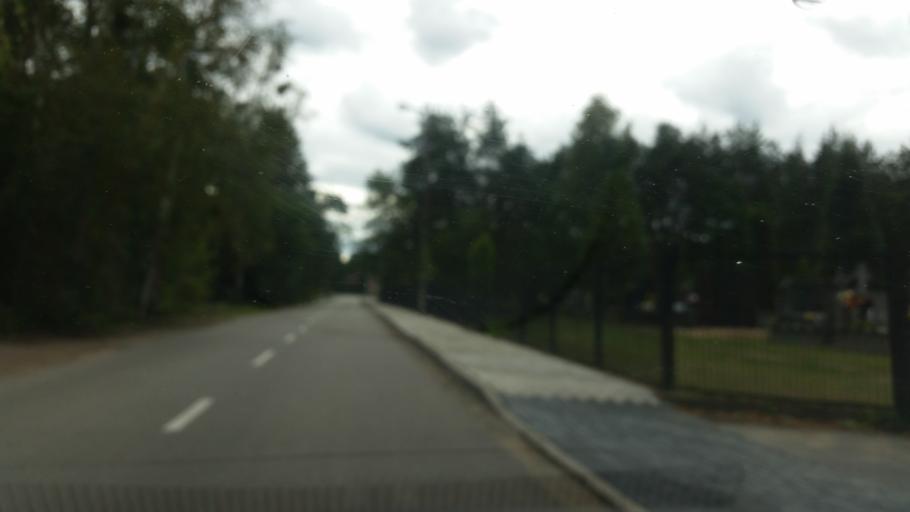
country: PL
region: Masovian Voivodeship
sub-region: Powiat piaseczynski
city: Konstancin-Jeziorna
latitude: 52.0658
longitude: 21.0992
